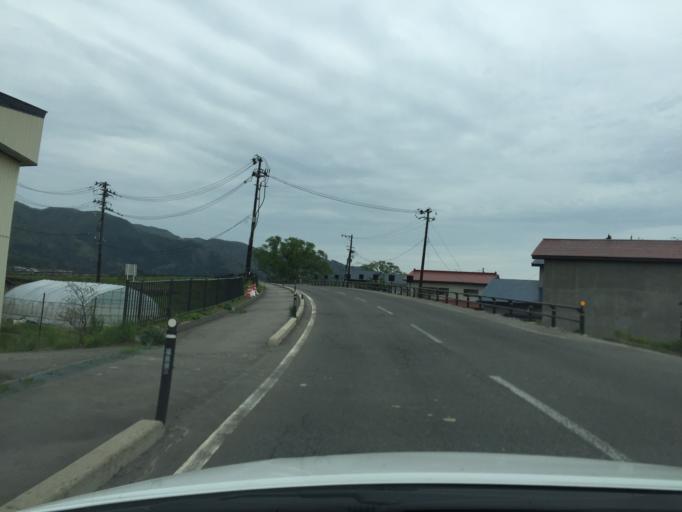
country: JP
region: Fukushima
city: Inawashiro
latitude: 37.5440
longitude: 140.1272
